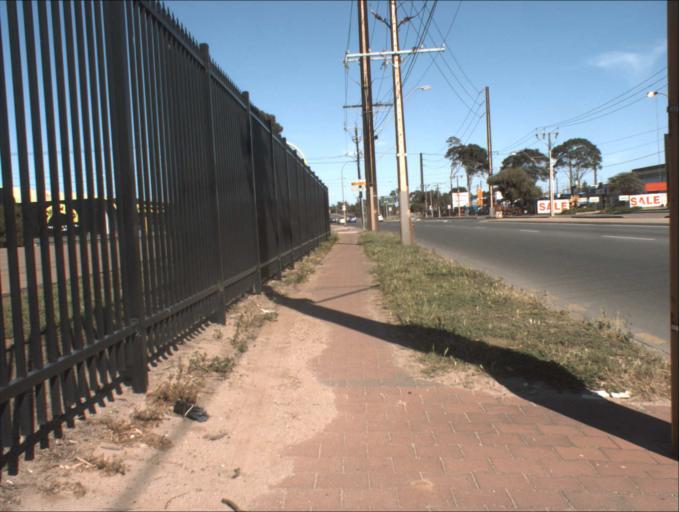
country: AU
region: South Australia
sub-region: Port Adelaide Enfield
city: Blair Athol
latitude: -34.8489
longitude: 138.5856
